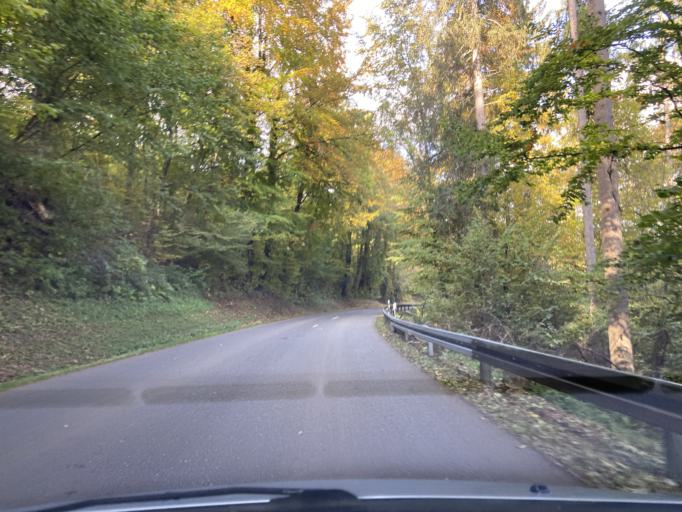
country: DE
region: Baden-Wuerttemberg
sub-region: Tuebingen Region
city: Sigmaringen
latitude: 48.0772
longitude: 9.2252
